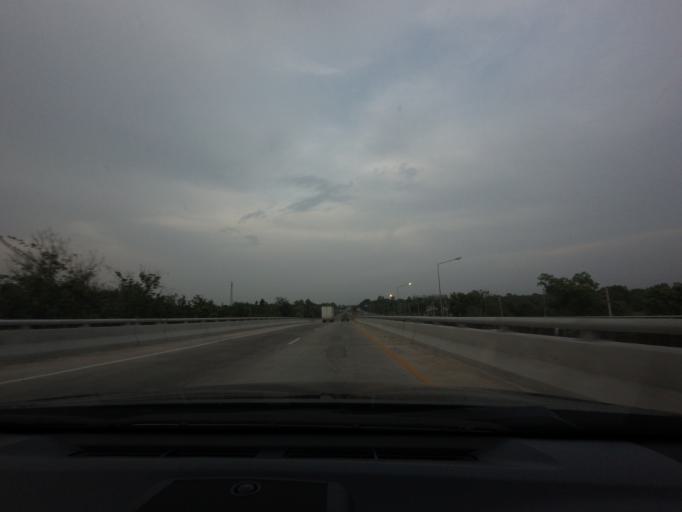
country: TH
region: Surat Thani
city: Phunphin
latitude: 9.1541
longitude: 99.1643
